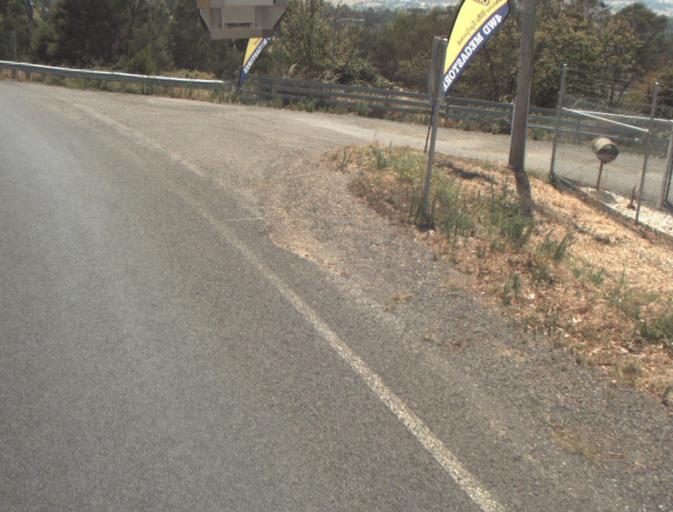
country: AU
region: Tasmania
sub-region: Launceston
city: Summerhill
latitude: -41.4971
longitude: 147.1721
